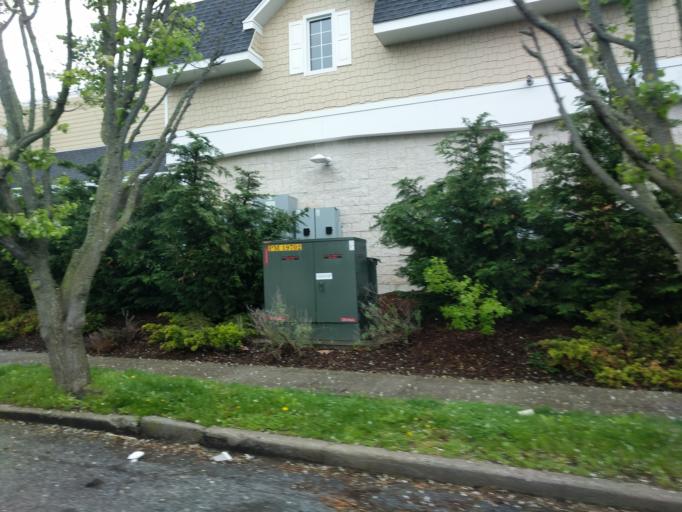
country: US
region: New York
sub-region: Nassau County
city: Island Park
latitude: 40.5983
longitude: -73.6544
